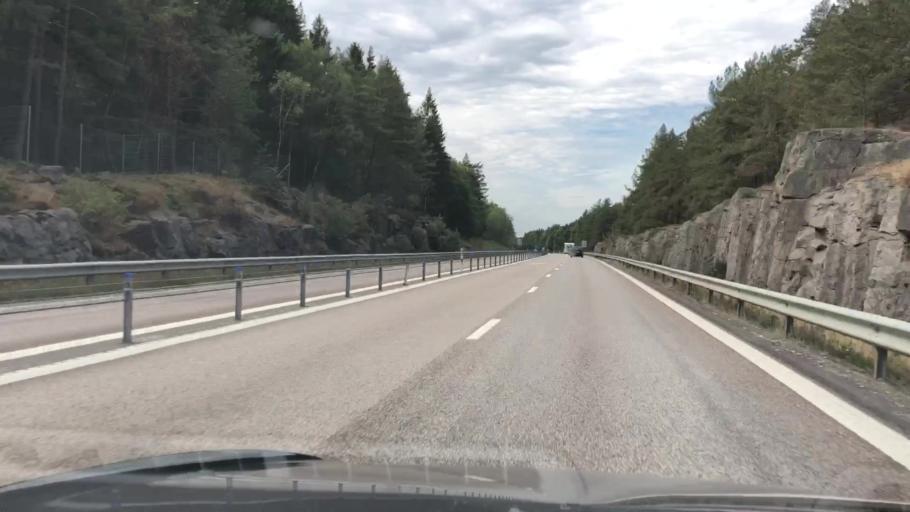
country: SE
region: Blekinge
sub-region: Ronneby Kommun
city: Brakne-Hoby
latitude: 56.2210
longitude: 15.1477
